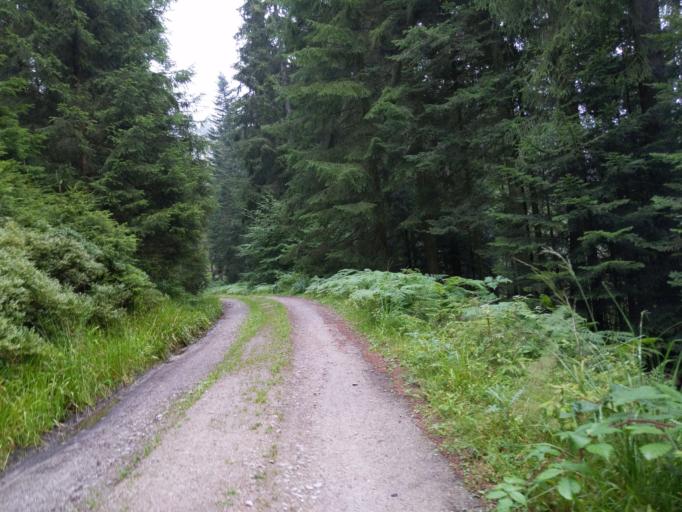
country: DE
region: Baden-Wuerttemberg
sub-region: Karlsruhe Region
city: Forbach
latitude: 48.6678
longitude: 8.2948
